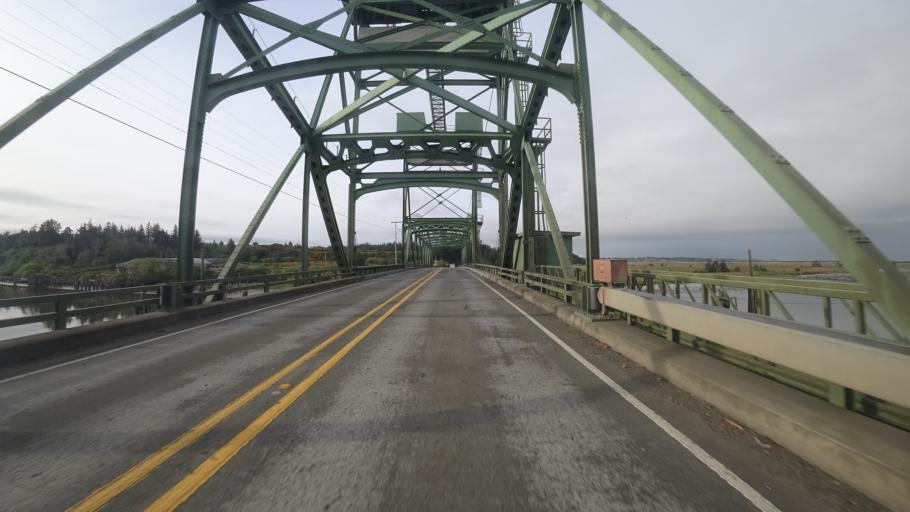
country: US
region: Oregon
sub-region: Coos County
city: Bandon
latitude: 43.1475
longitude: -124.3955
